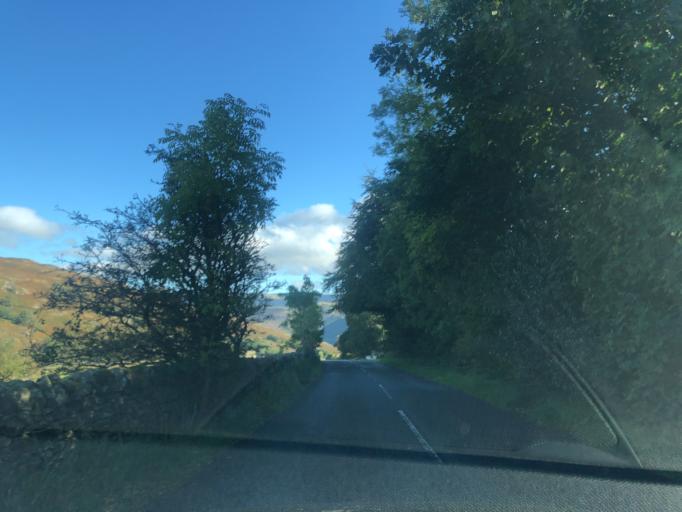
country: GB
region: England
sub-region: Cumbria
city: Ambleside
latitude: 54.5822
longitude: -2.9356
